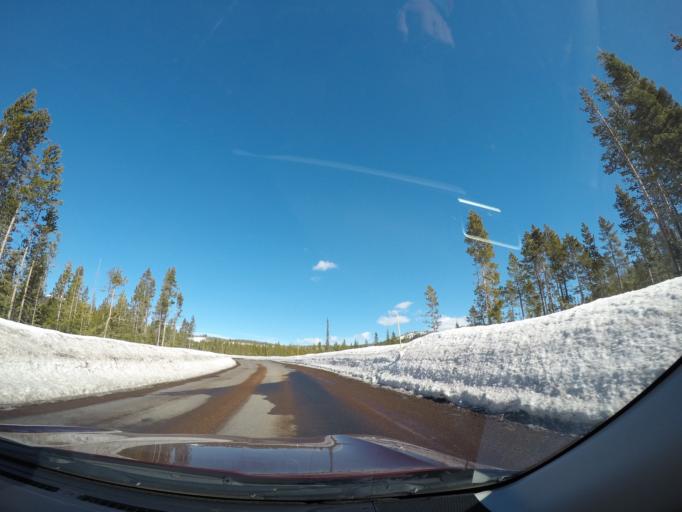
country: US
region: Oregon
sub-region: Deschutes County
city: Sunriver
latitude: 43.9755
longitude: -121.6099
